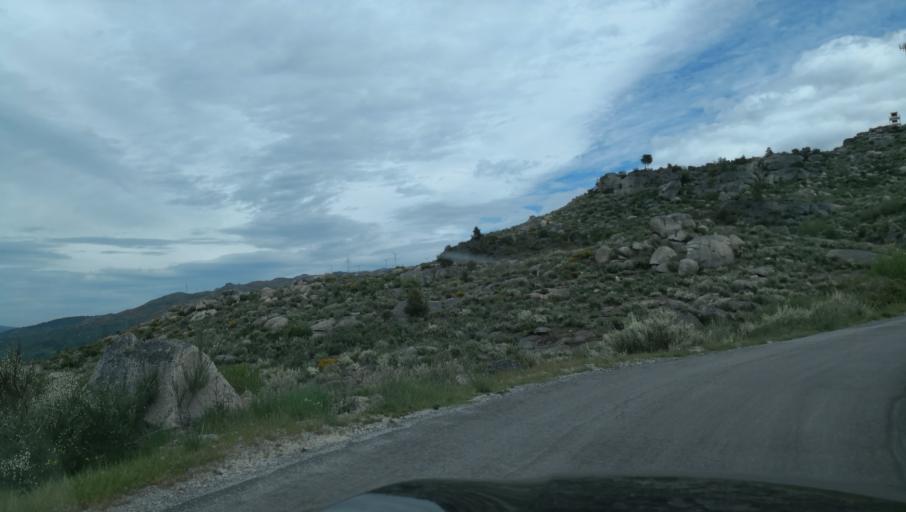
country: PT
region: Vila Real
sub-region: Vila Real
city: Vila Real
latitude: 41.3740
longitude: -7.6938
